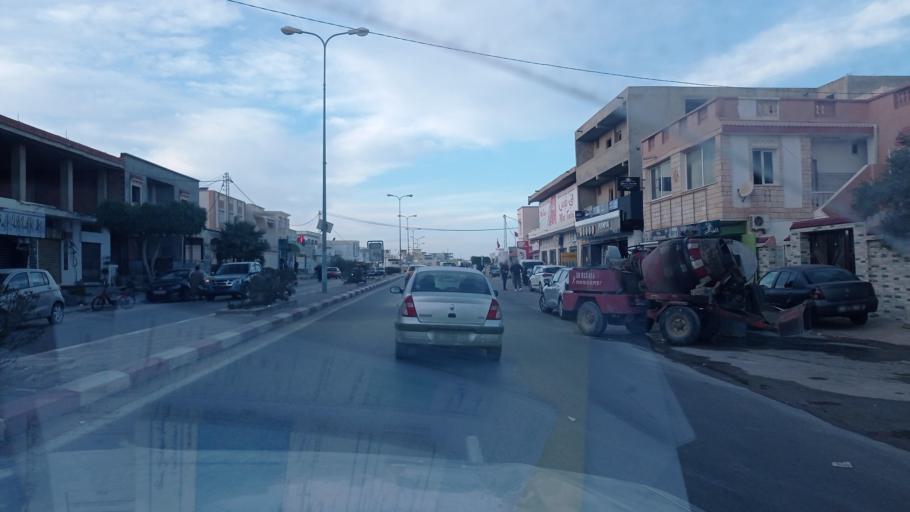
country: TN
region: Qabis
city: Gabes
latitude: 33.8470
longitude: 10.1128
